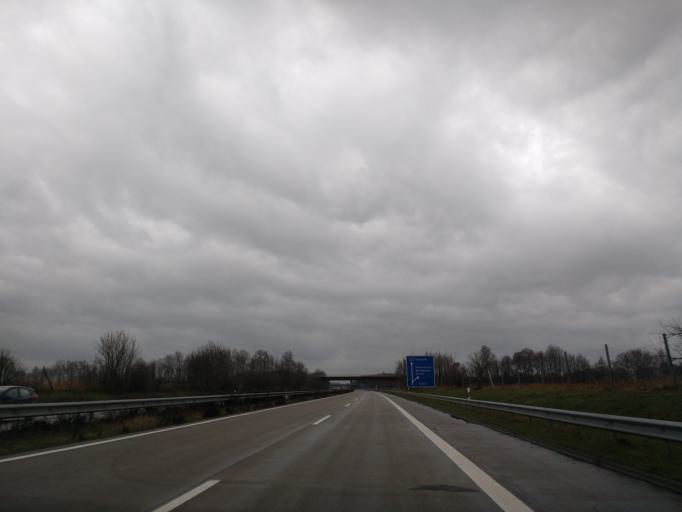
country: DE
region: Lower Saxony
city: Midlum
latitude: 53.6842
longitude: 8.6588
